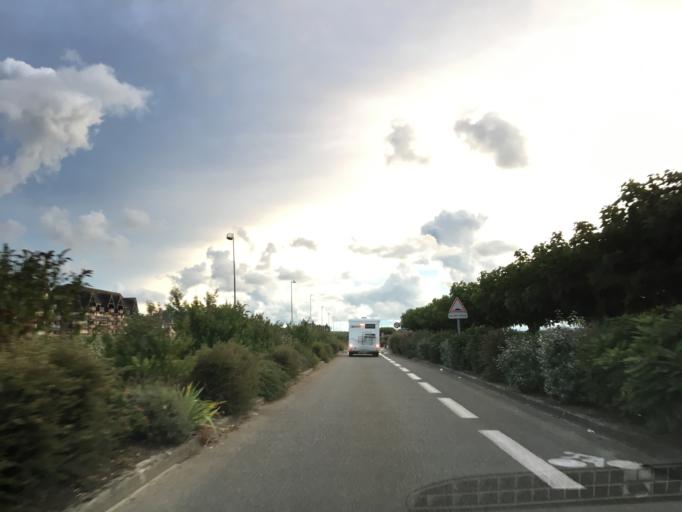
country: FR
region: Lower Normandy
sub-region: Departement du Calvados
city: Deauville
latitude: 49.3574
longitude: 0.0639
